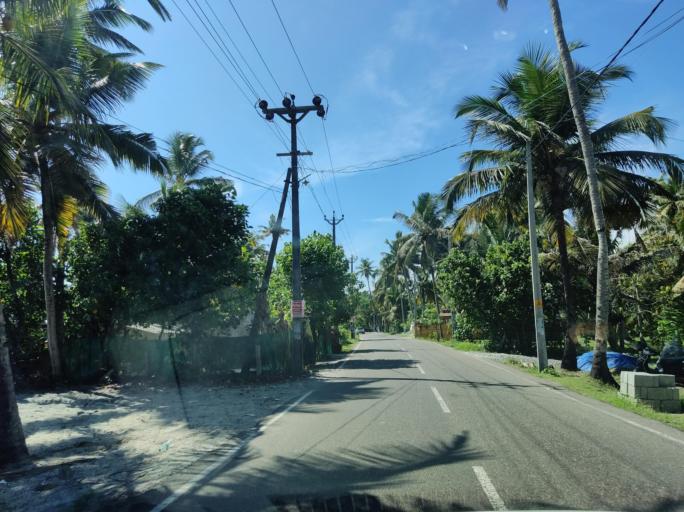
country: IN
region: Kerala
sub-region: Alappuzha
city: Kayankulam
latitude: 9.1947
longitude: 76.4371
